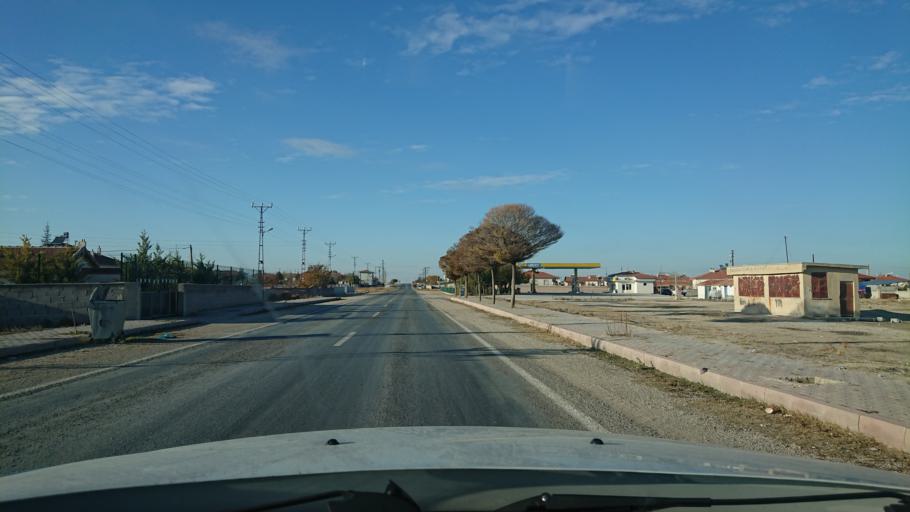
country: TR
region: Aksaray
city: Eskil
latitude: 38.5662
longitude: 33.1933
